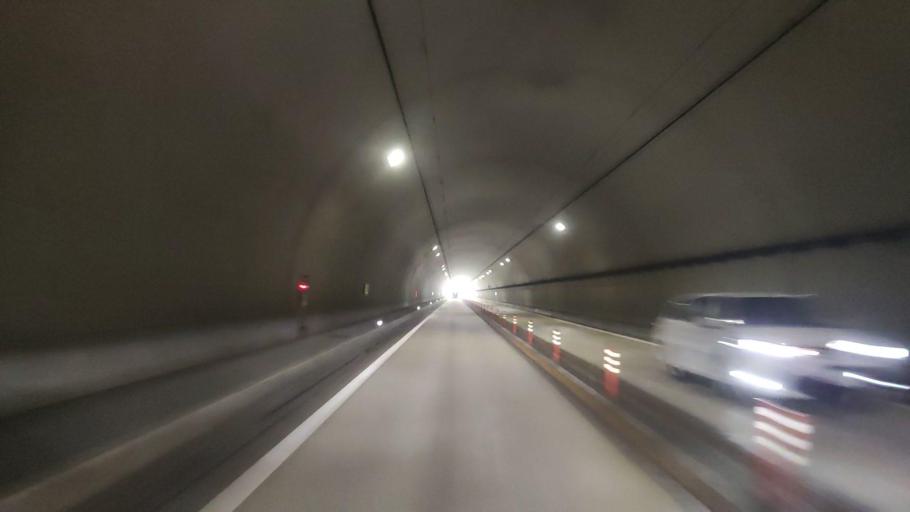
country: JP
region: Wakayama
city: Tanabe
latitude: 33.5646
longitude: 135.4977
